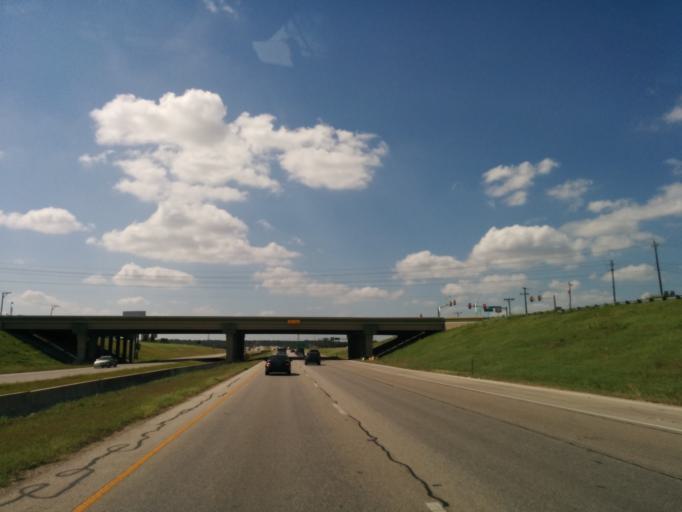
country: US
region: Texas
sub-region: Bexar County
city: Live Oak
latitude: 29.5909
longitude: -98.3511
